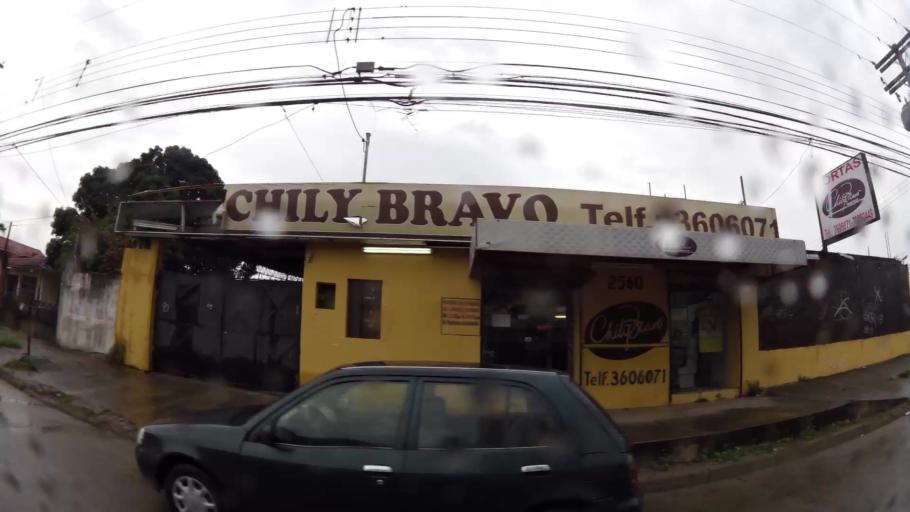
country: BO
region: Santa Cruz
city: Santa Cruz de la Sierra
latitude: -17.7721
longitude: -63.1590
